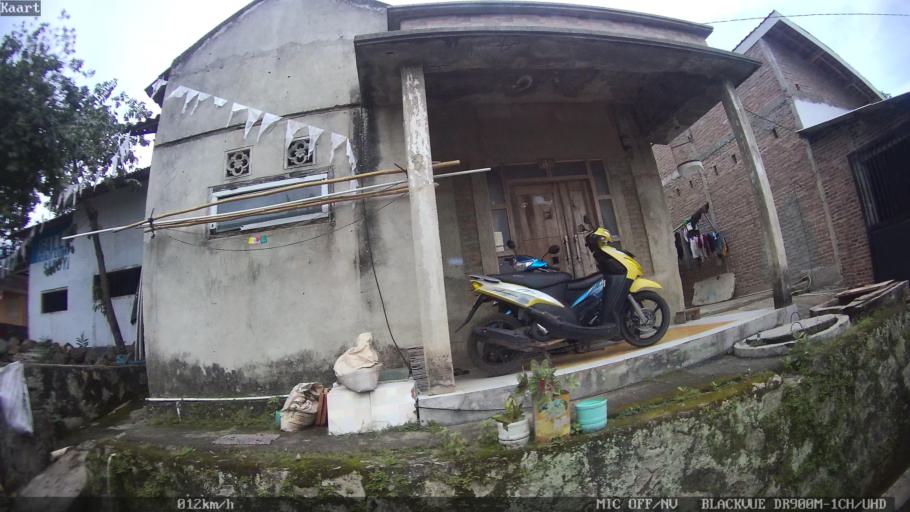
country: ID
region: Lampung
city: Kedaton
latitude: -5.3891
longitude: 105.2001
